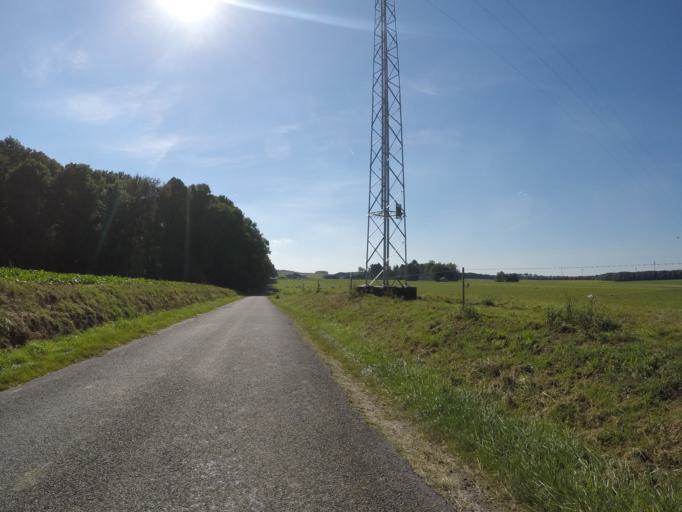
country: BE
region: Wallonia
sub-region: Province de Namur
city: Assesse
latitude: 50.3056
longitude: 5.0311
